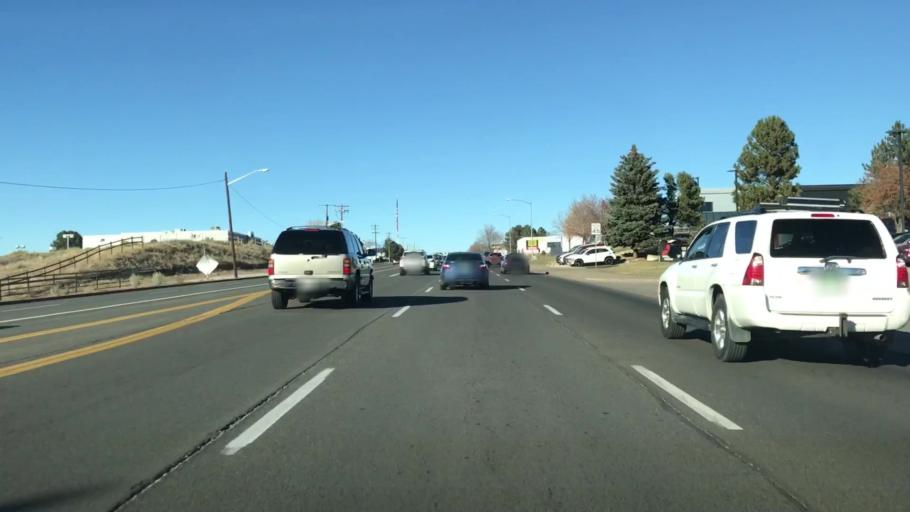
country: US
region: Colorado
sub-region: Adams County
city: Aurora
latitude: 39.6625
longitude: -104.8662
